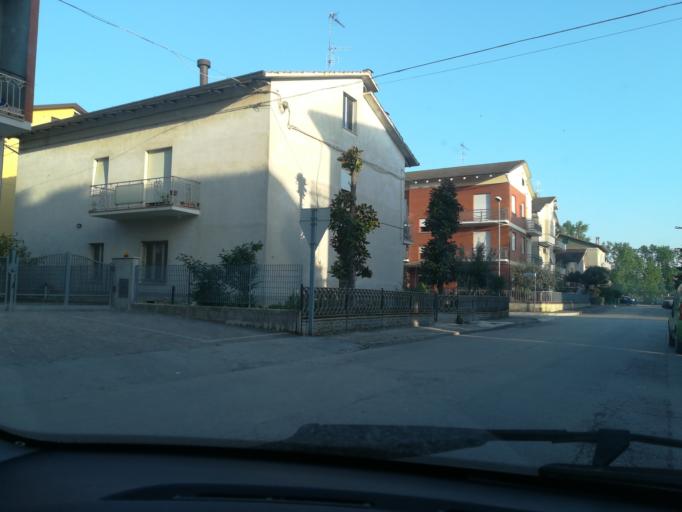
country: IT
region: The Marches
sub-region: Provincia di Macerata
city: Piediripa
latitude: 43.2744
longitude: 13.5015
